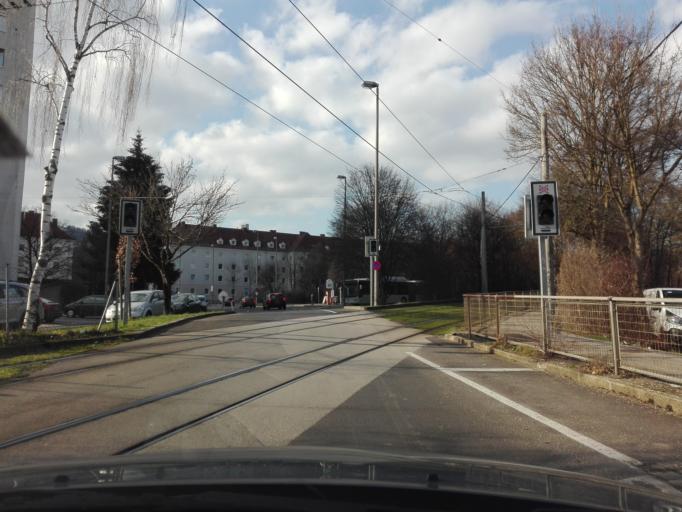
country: AT
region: Upper Austria
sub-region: Linz Stadt
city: Linz
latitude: 48.3230
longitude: 14.2846
